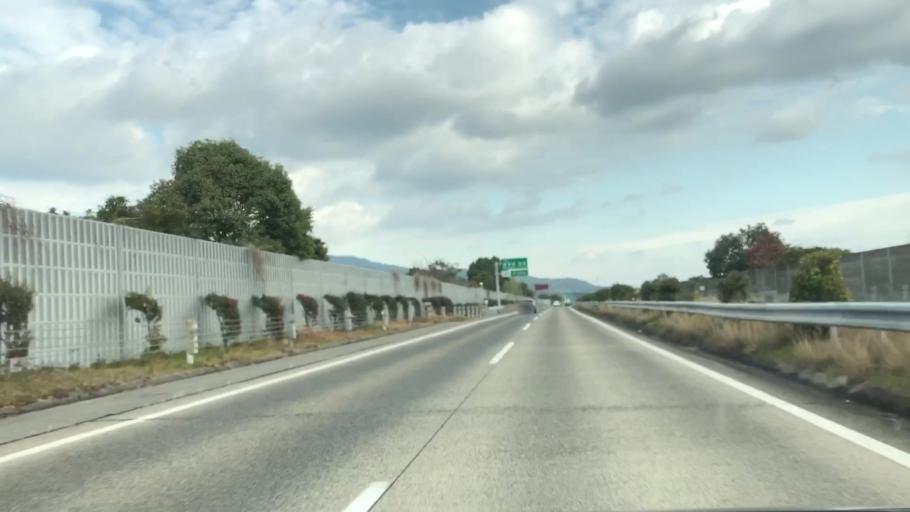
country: JP
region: Saga Prefecture
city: Kanzakimachi-kanzaki
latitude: 33.3526
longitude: 130.3857
